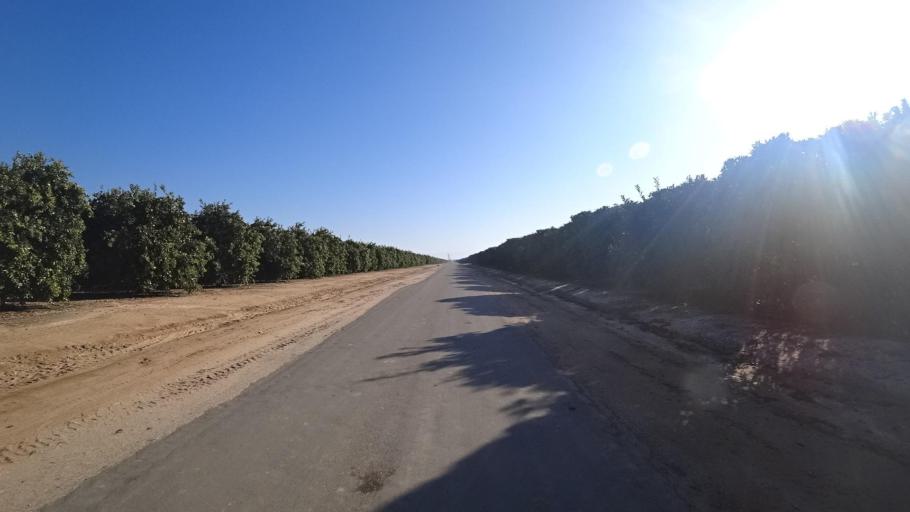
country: US
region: California
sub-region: Tulare County
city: Richgrove
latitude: 35.7252
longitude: -119.1402
